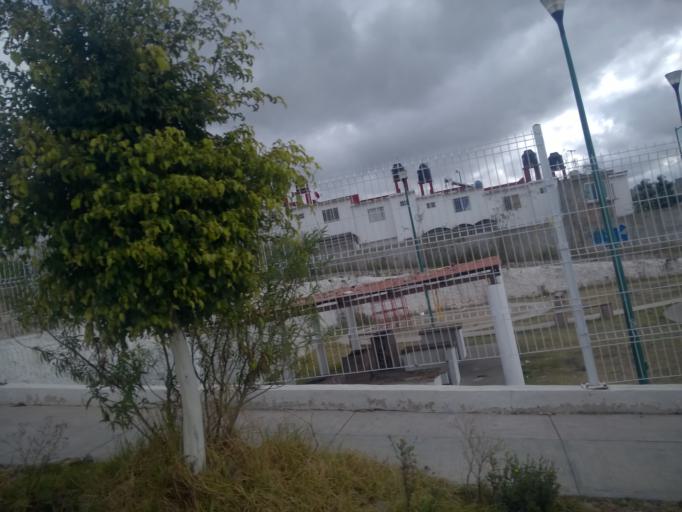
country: MX
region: Guanajuato
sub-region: Leon
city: La Ermita
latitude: 21.1593
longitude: -101.7388
